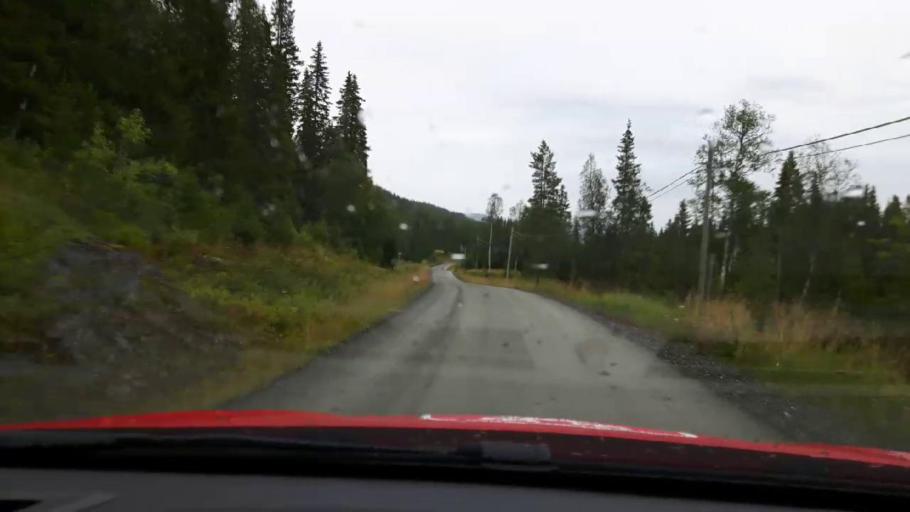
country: SE
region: Jaemtland
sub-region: Are Kommun
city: Are
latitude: 63.5035
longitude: 12.7478
